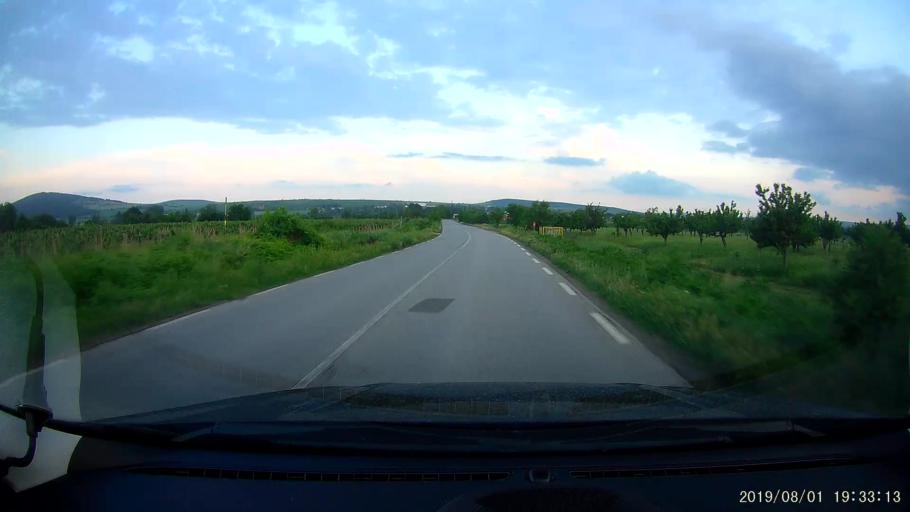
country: BG
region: Burgas
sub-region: Obshtina Sungurlare
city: Sungurlare
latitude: 42.7836
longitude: 26.8752
